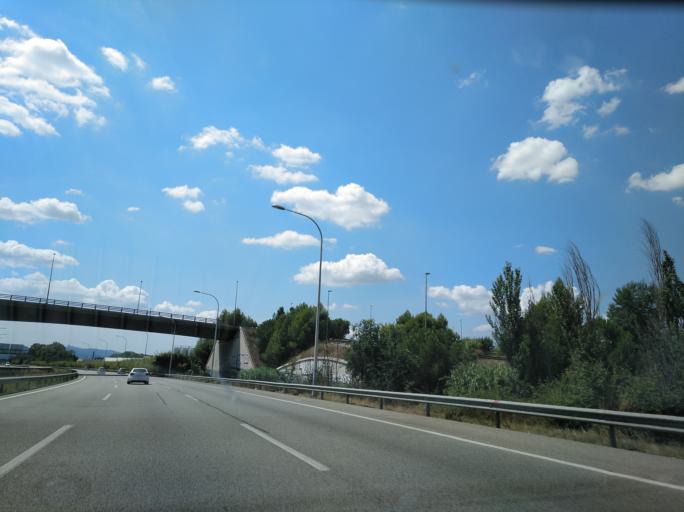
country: ES
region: Catalonia
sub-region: Provincia de Barcelona
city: Mollet del Valles
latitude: 41.5420
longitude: 2.2281
